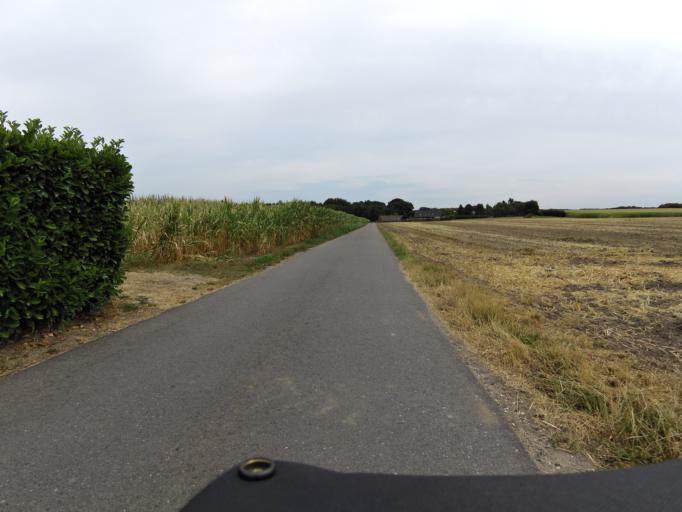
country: DE
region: North Rhine-Westphalia
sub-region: Regierungsbezirk Dusseldorf
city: Weeze
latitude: 51.5884
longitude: 6.1788
